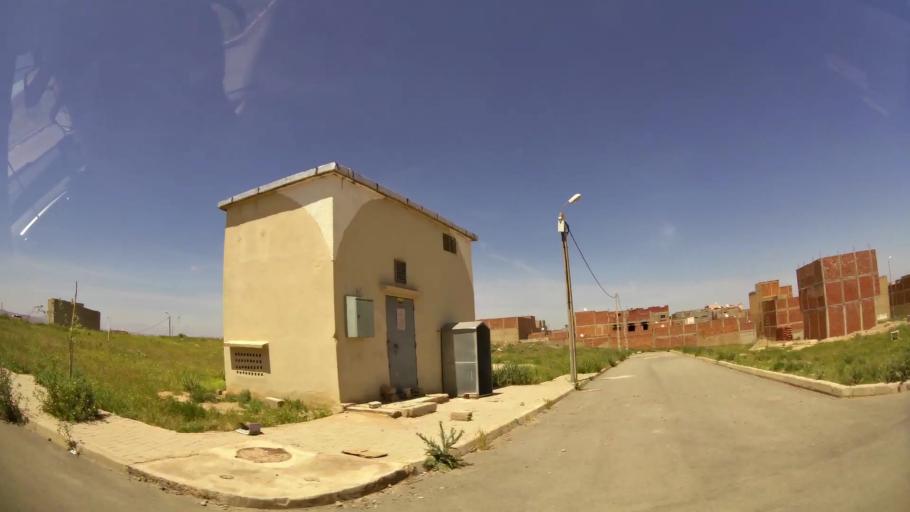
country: MA
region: Oriental
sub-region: Oujda-Angad
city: Oujda
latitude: 34.6558
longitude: -1.9276
